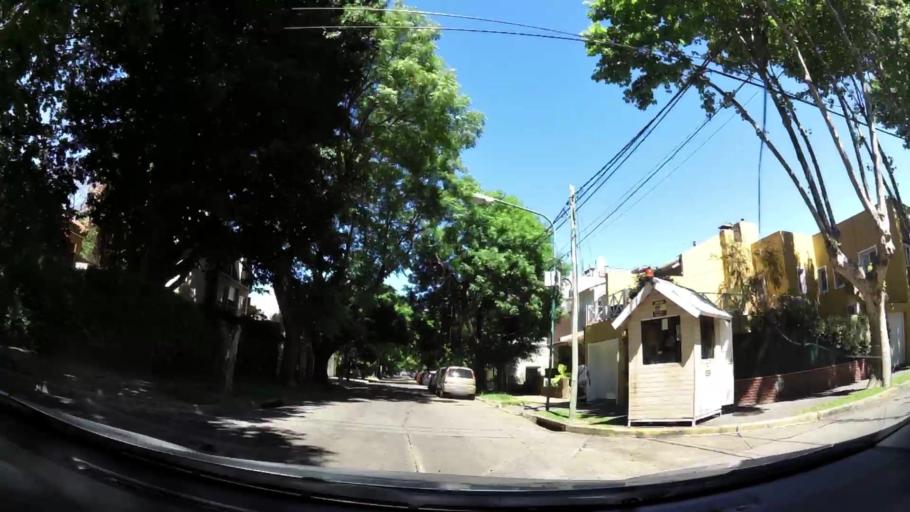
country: AR
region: Buenos Aires
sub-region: Partido de Vicente Lopez
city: Olivos
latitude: -34.5008
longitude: -58.4885
